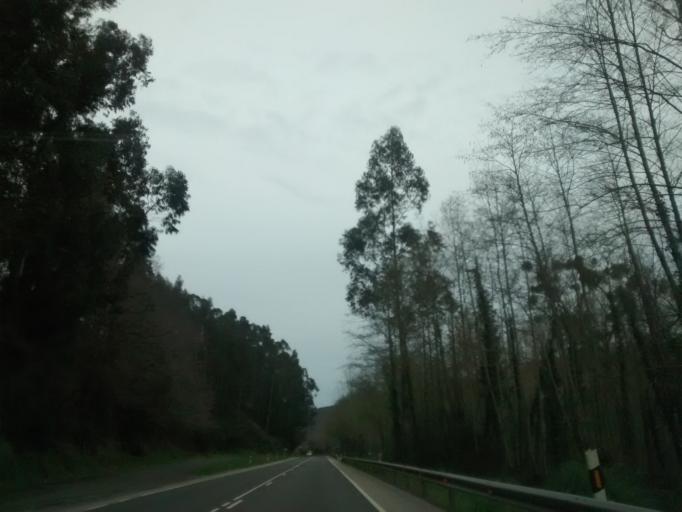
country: ES
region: Cantabria
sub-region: Provincia de Cantabria
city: Puente Viesgo
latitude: 43.3130
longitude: -3.9592
